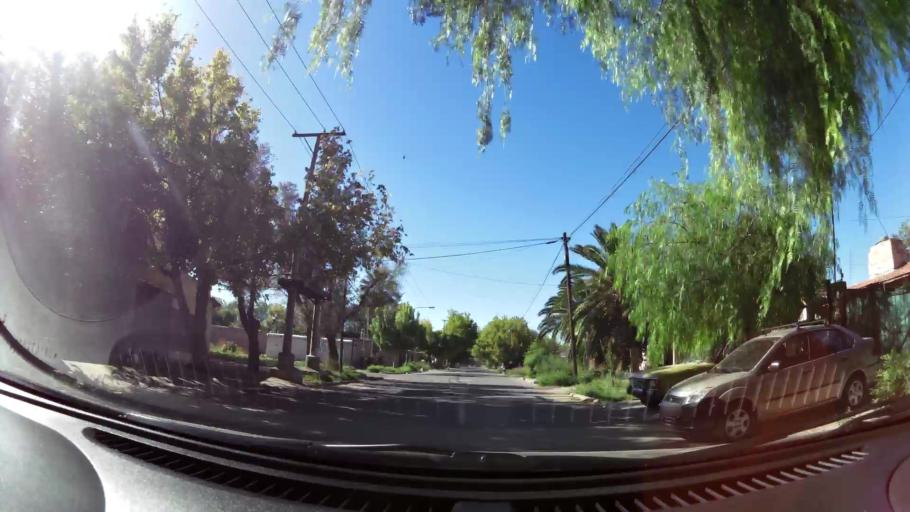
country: AR
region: Mendoza
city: Las Heras
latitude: -32.8379
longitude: -68.8297
